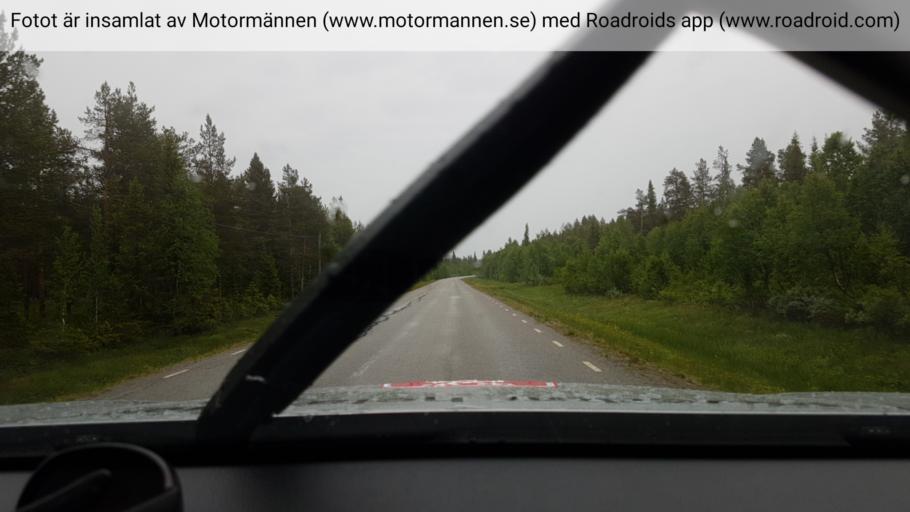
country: SE
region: Vaesterbotten
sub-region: Storumans Kommun
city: Fristad
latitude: 65.8817
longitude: 16.3940
